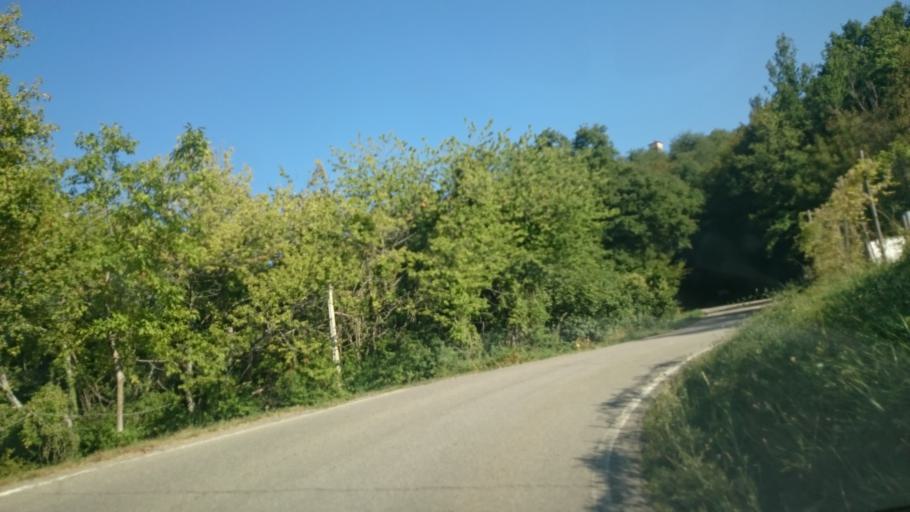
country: IT
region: Emilia-Romagna
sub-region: Provincia di Reggio Emilia
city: Villa Minozzo
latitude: 44.3494
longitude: 10.4890
